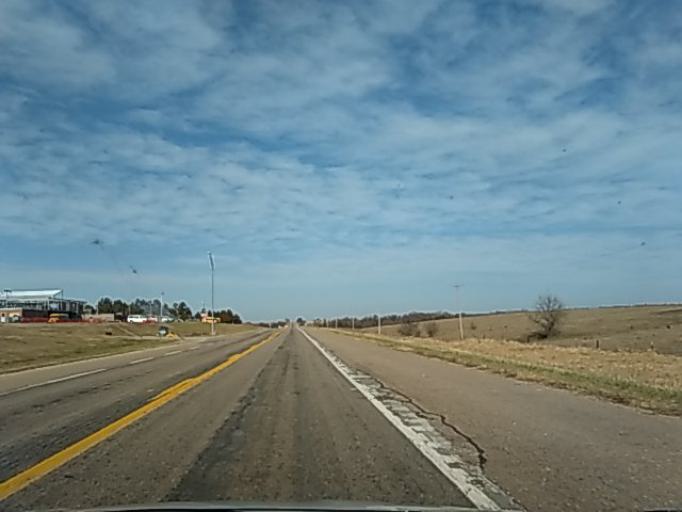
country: US
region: Nebraska
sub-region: Clay County
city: Clay Center
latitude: 40.4304
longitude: -98.0514
